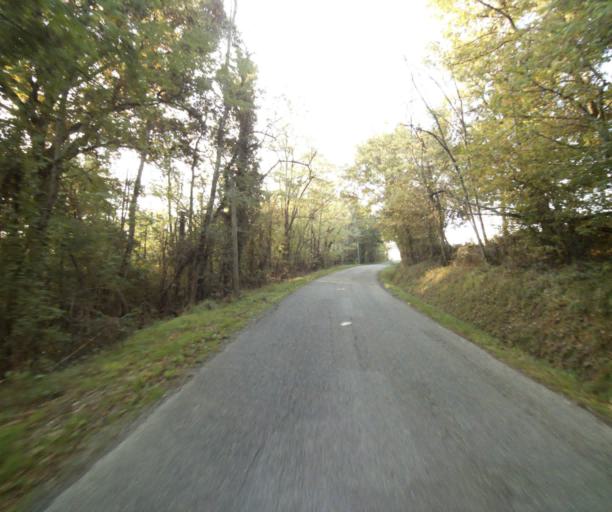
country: FR
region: Midi-Pyrenees
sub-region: Departement du Tarn-et-Garonne
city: Saint-Nauphary
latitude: 43.9368
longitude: 1.4415
